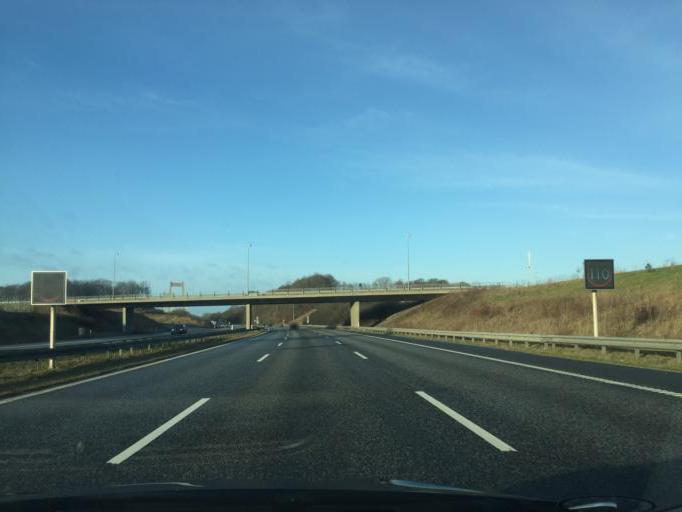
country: DK
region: South Denmark
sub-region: Middelfart Kommune
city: Strib
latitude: 55.5129
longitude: 9.7753
